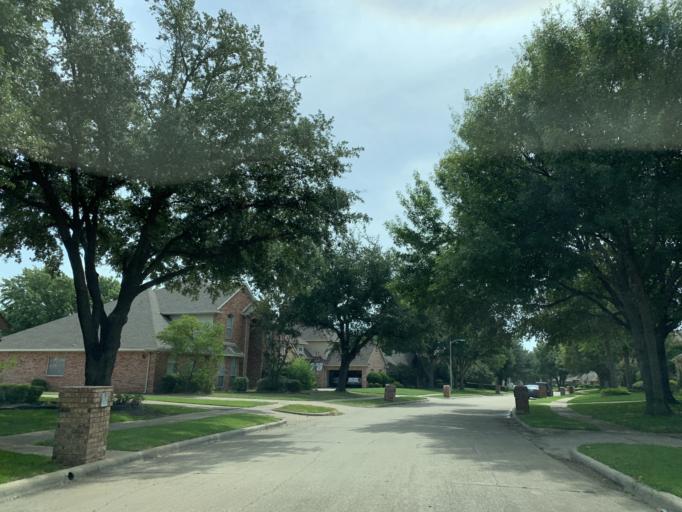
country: US
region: Texas
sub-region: Dallas County
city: Grand Prairie
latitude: 32.6683
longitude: -97.0008
